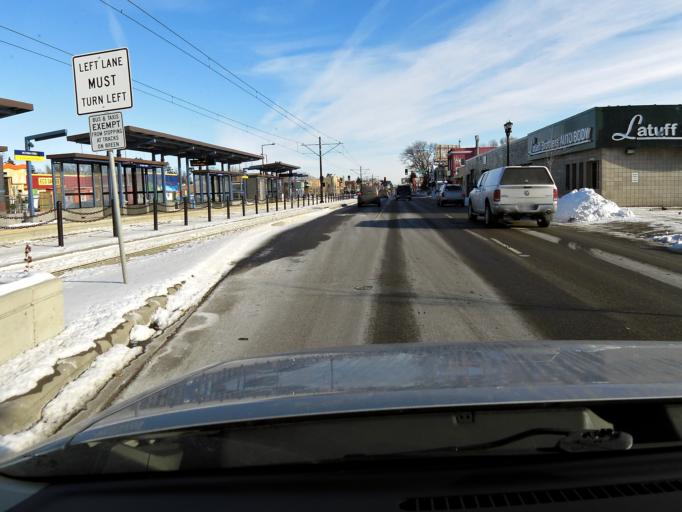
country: US
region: Minnesota
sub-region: Ramsey County
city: Saint Paul
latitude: 44.9556
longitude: -93.1378
